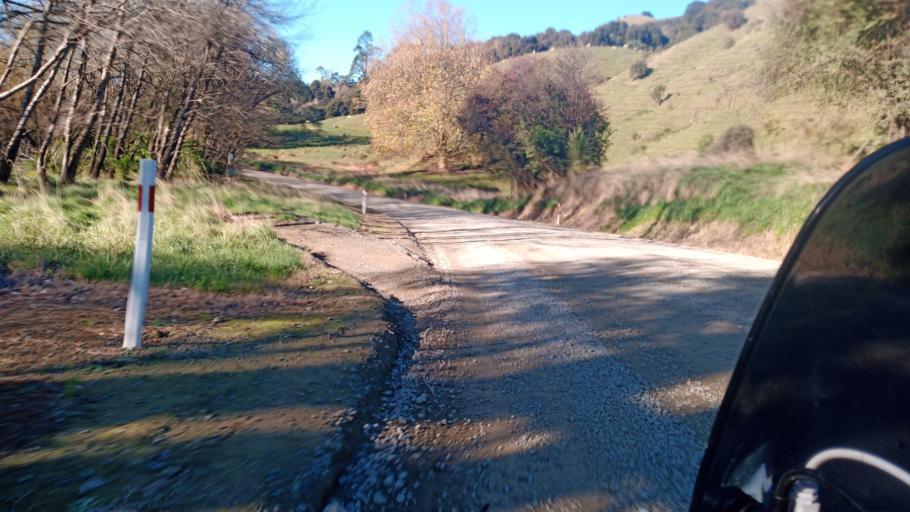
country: NZ
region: Hawke's Bay
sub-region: Wairoa District
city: Wairoa
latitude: -38.8481
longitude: 177.1660
